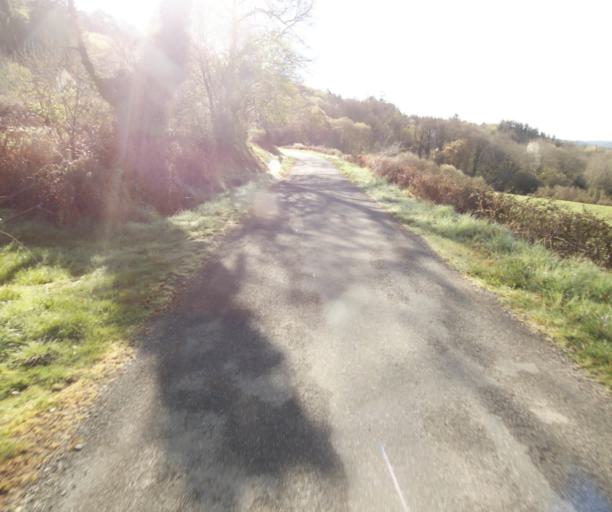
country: FR
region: Limousin
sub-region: Departement de la Correze
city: Laguenne
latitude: 45.2616
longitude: 1.8502
